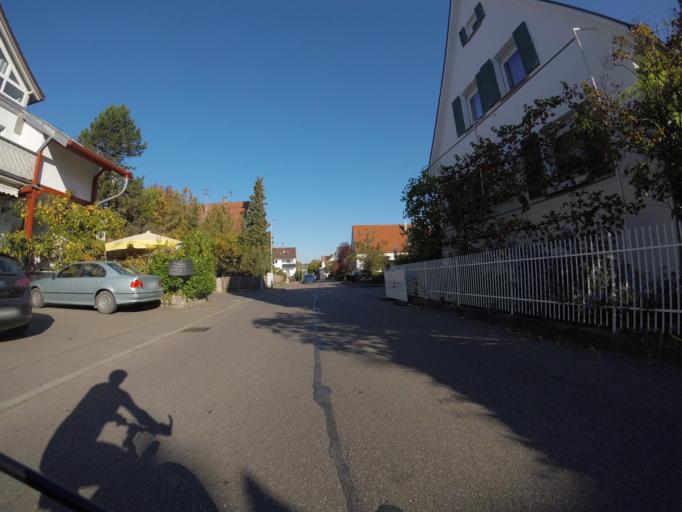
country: DE
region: Baden-Wuerttemberg
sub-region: Regierungsbezirk Stuttgart
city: Murr
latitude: 48.9627
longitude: 9.2576
